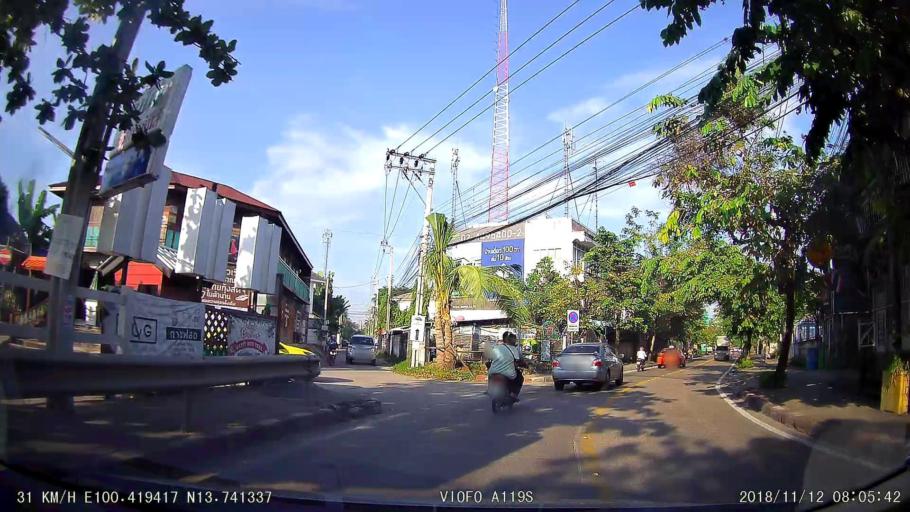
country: TH
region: Bangkok
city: Phasi Charoen
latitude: 13.7413
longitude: 100.4193
